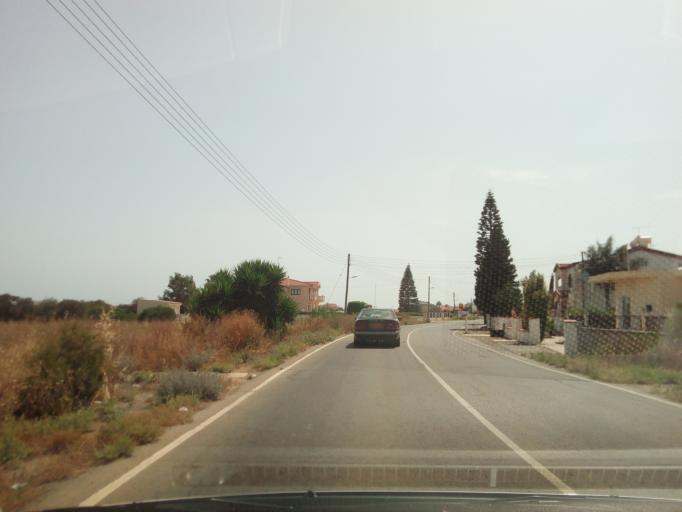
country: CY
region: Larnaka
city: Perivolia
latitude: 34.8364
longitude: 33.5874
